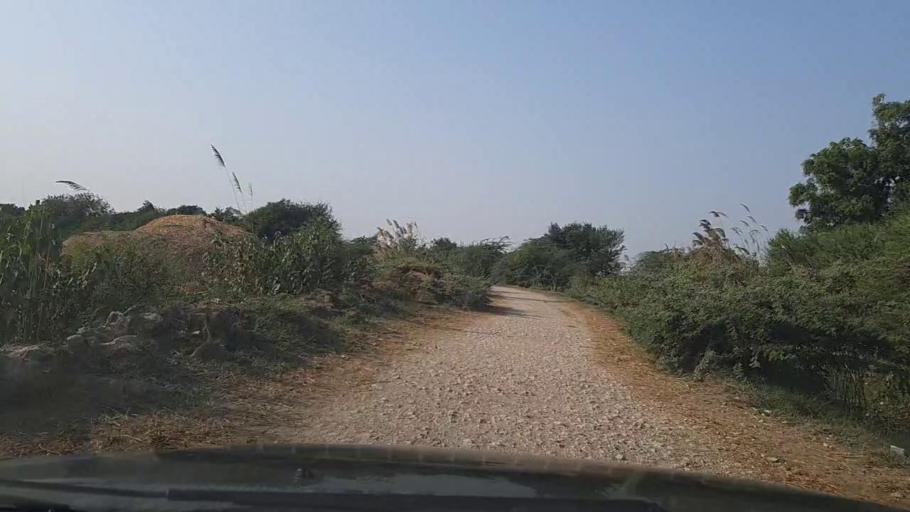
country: PK
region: Sindh
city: Mirpur Sakro
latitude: 24.6383
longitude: 67.7498
